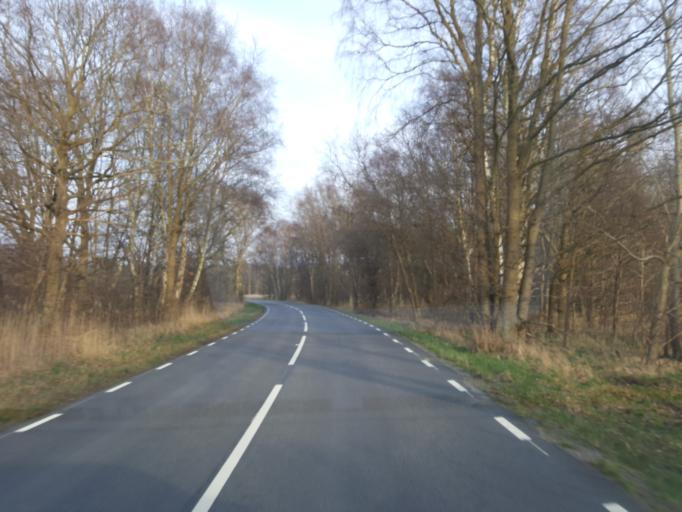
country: SE
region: Skane
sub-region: Simrishamns Kommun
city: Simrishamn
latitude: 55.3932
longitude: 14.1680
